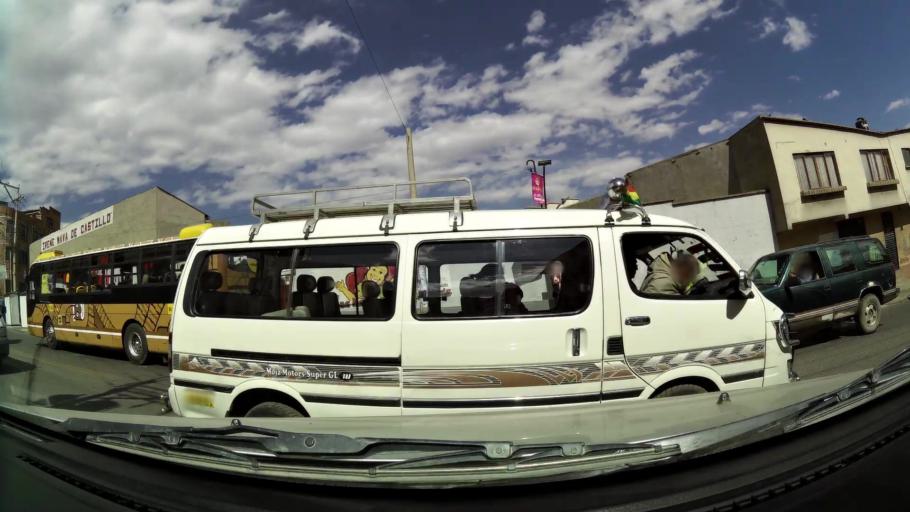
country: BO
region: La Paz
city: La Paz
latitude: -16.4677
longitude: -68.1135
